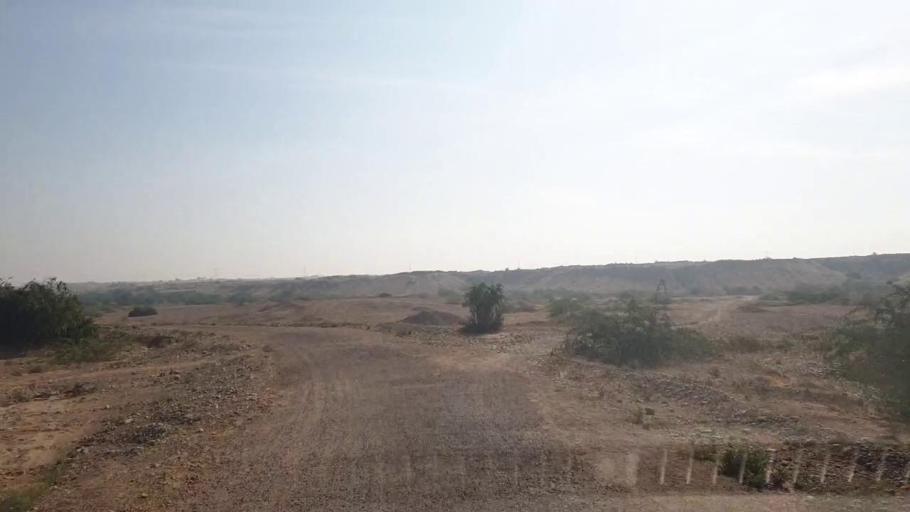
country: PK
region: Sindh
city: Matiari
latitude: 25.6226
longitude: 68.3182
